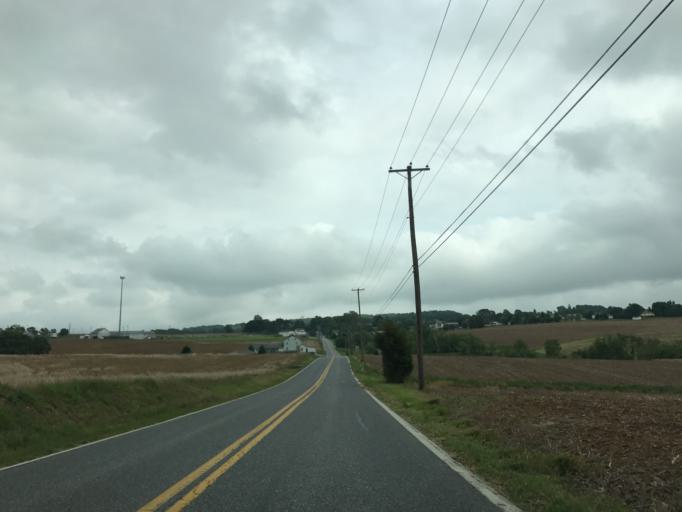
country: US
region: Pennsylvania
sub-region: York County
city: Dallastown
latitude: 39.8391
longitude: -76.6261
